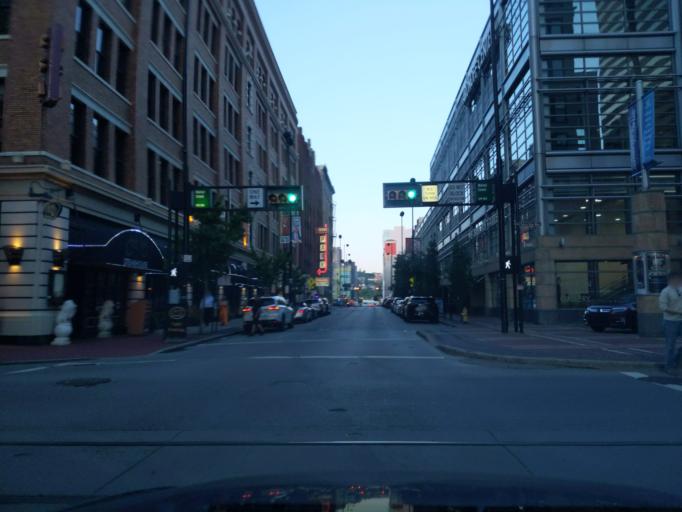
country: US
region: Kentucky
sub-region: Campbell County
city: Newport
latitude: 39.1039
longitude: -84.5121
